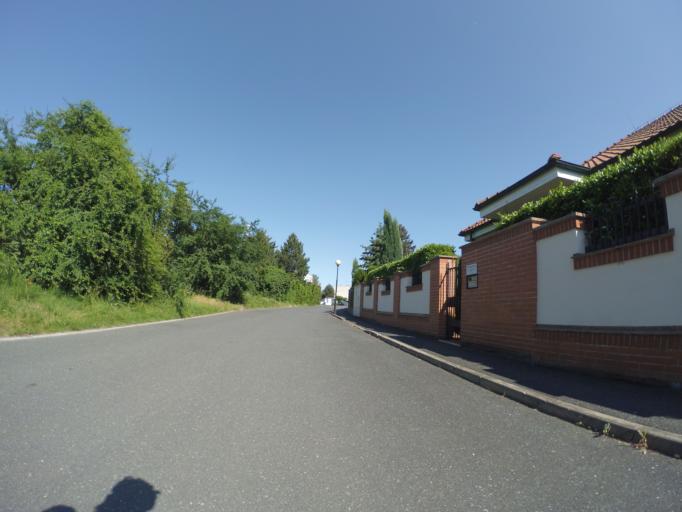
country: CZ
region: Central Bohemia
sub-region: Okres Nymburk
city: Podebrady
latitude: 50.1533
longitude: 15.1085
